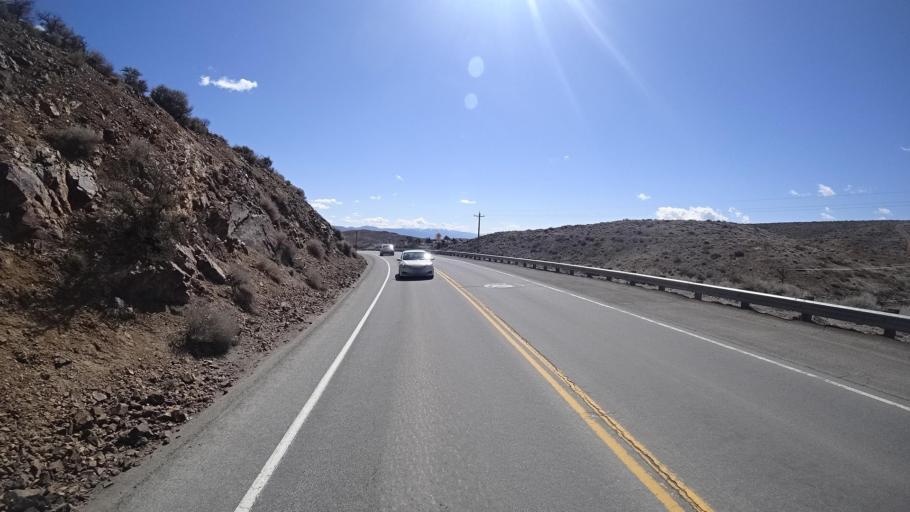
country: US
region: Nevada
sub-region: Washoe County
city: Golden Valley
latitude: 39.5881
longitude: -119.8344
